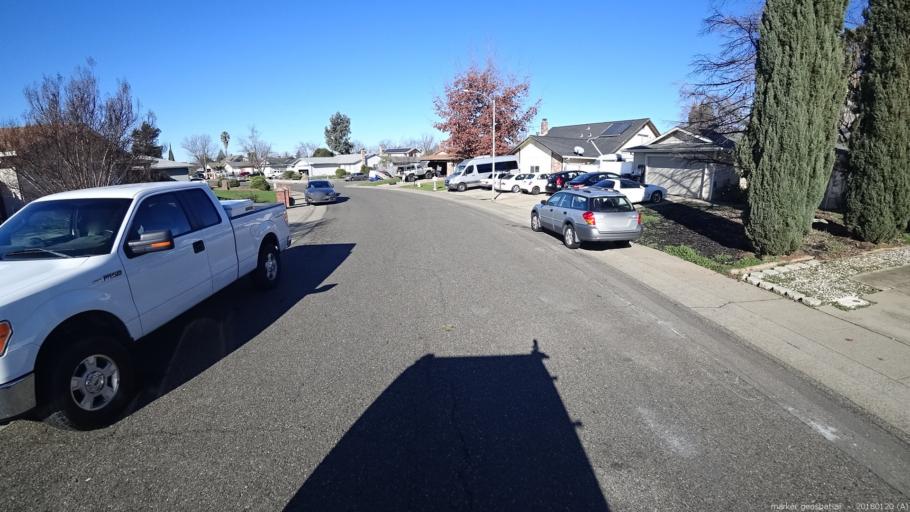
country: US
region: California
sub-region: Sacramento County
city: Rancho Cordova
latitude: 38.5750
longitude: -121.3101
